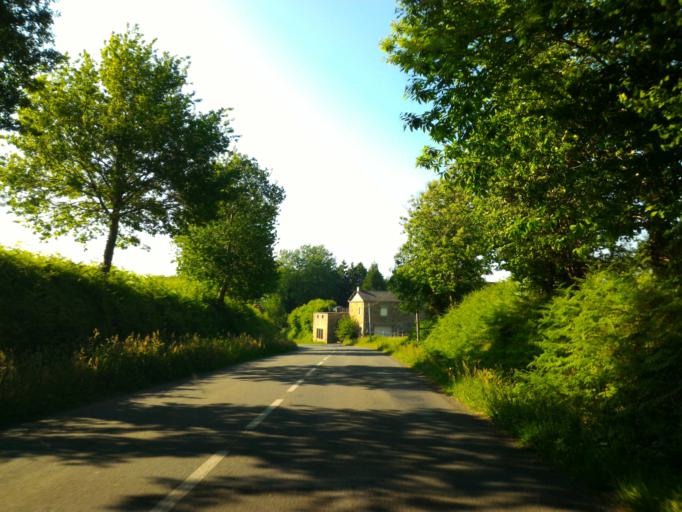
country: FR
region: Brittany
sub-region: Departement d'Ille-et-Vilaine
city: Luitre
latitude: 48.2727
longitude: -1.1490
